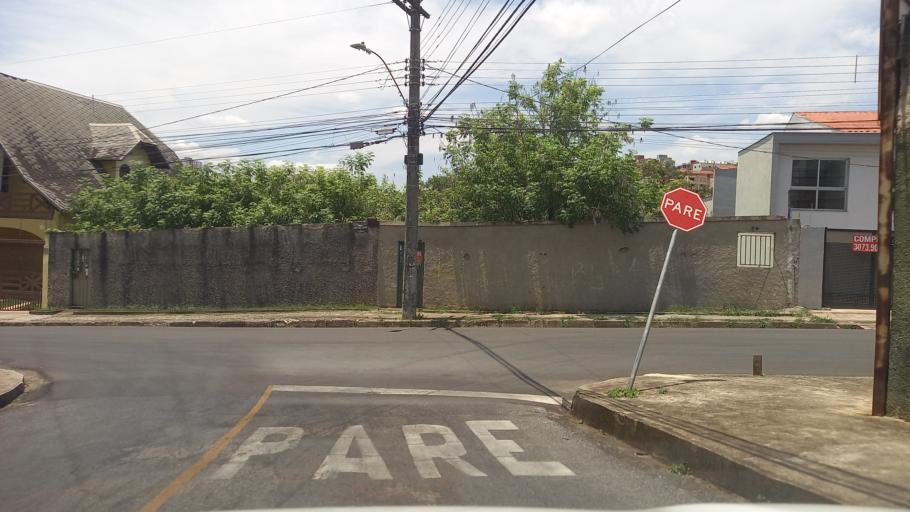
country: BR
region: Minas Gerais
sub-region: Contagem
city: Contagem
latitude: -19.9134
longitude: -44.0053
